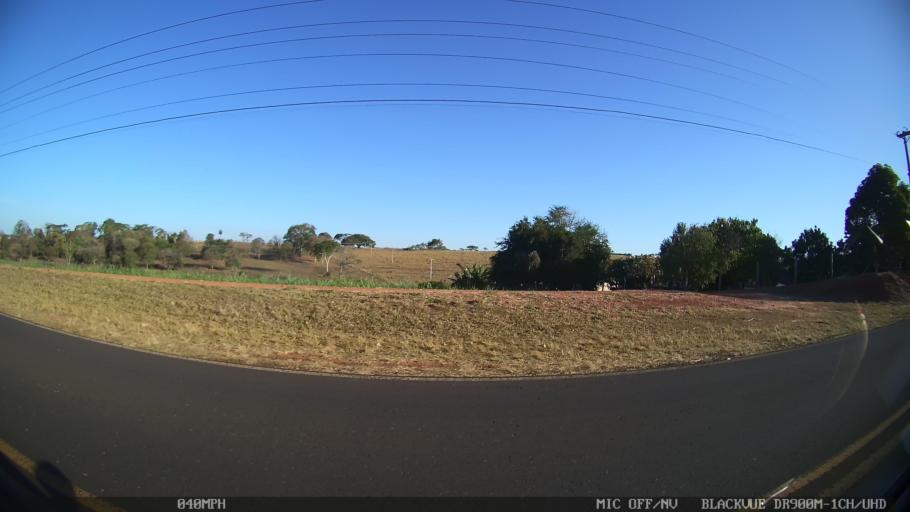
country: BR
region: Sao Paulo
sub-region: Guapiacu
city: Guapiacu
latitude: -20.7874
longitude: -49.2442
